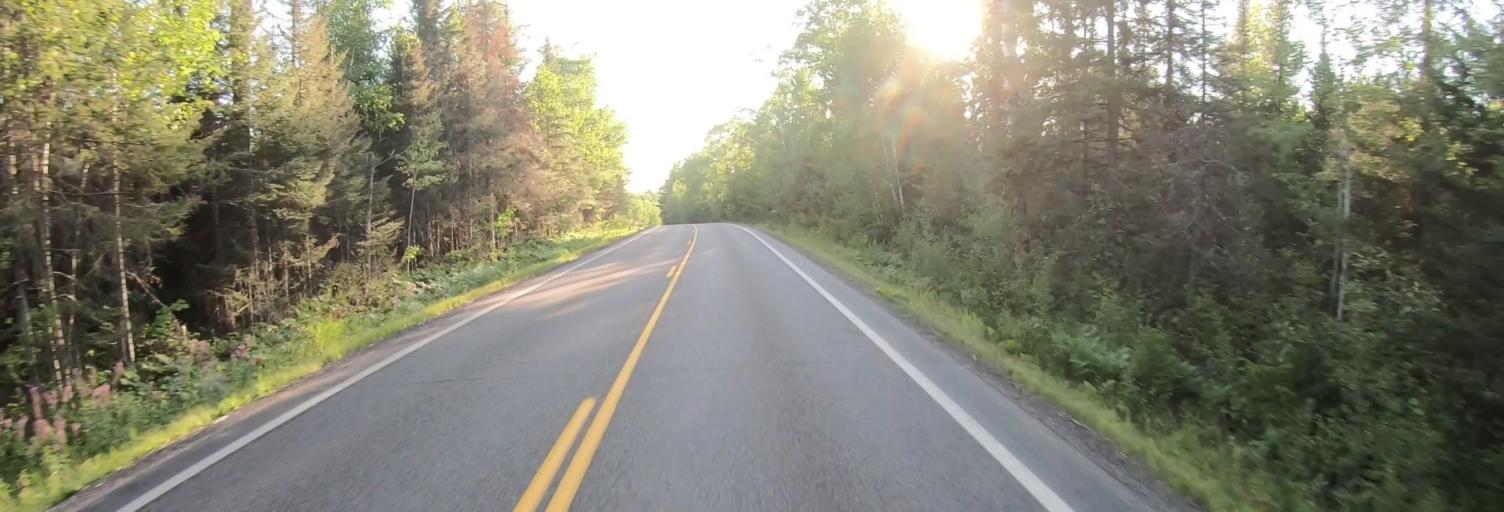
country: US
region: Minnesota
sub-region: Saint Louis County
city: Ely
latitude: 47.9579
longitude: -91.6090
